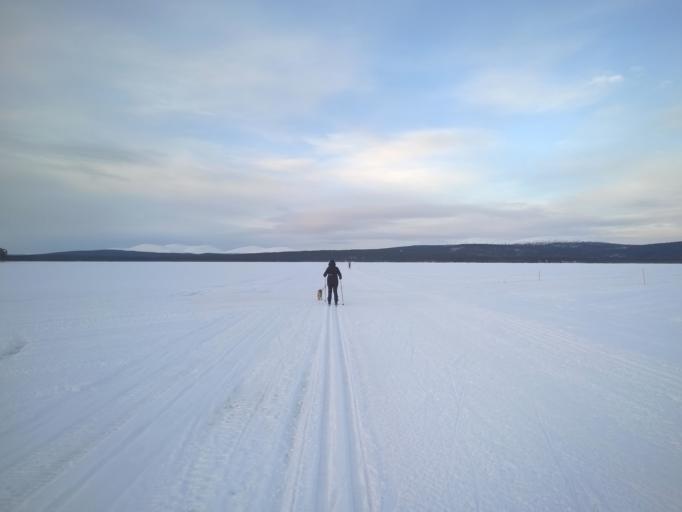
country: FI
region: Lapland
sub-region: Tunturi-Lappi
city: Muonio
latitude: 67.9222
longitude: 24.0173
